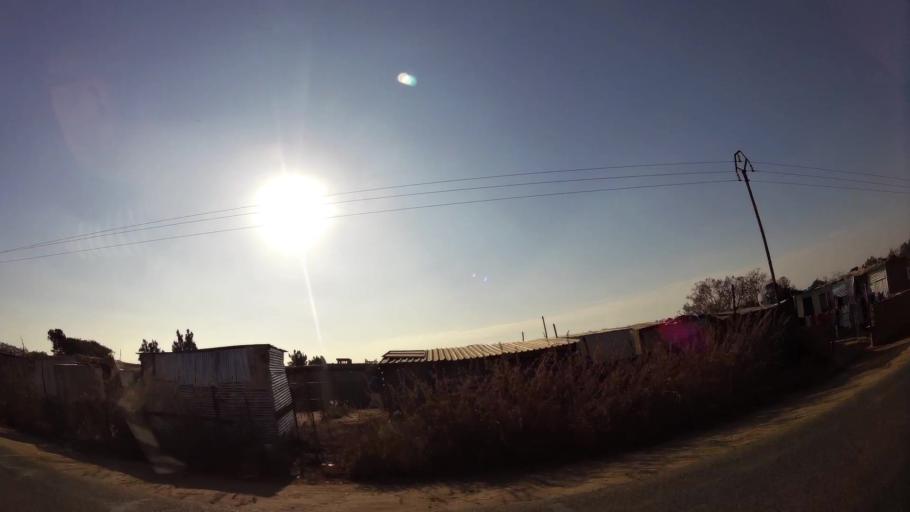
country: ZA
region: Gauteng
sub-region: West Rand District Municipality
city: Muldersdriseloop
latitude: -26.0222
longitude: 27.8761
